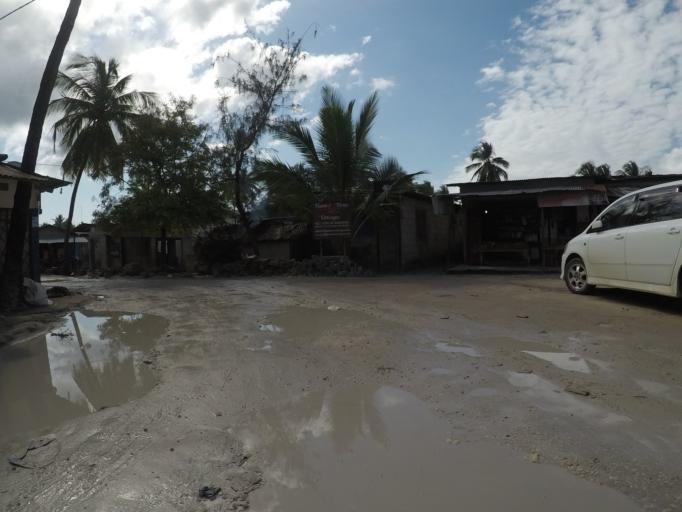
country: TZ
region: Zanzibar North
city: Nungwi
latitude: -5.7270
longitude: 39.2965
